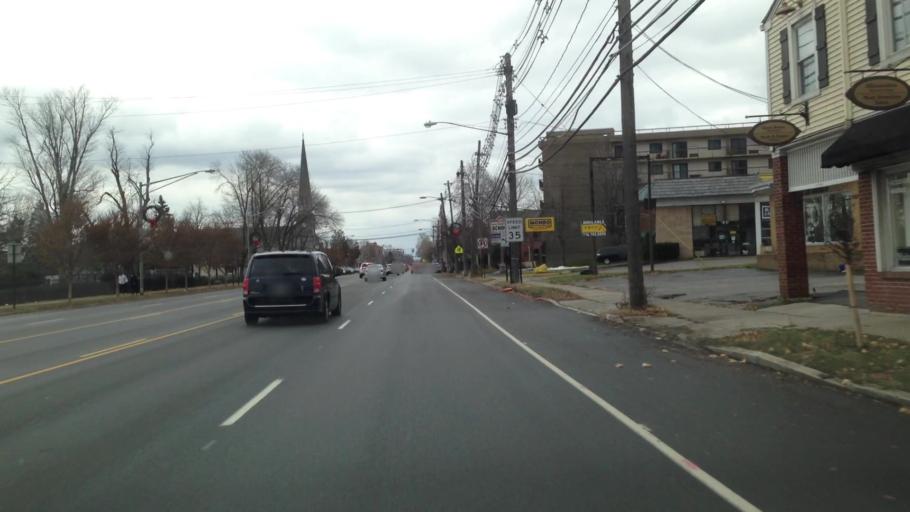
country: US
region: New York
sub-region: Erie County
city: Williamsville
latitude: 42.9614
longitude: -78.7534
